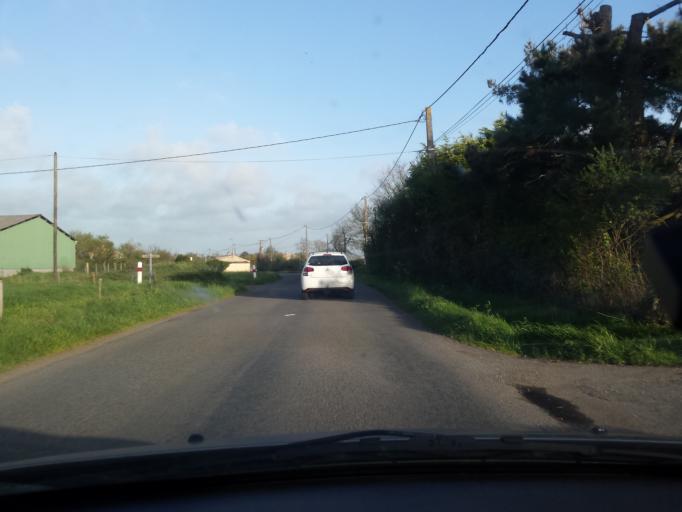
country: FR
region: Pays de la Loire
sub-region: Departement de la Vendee
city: Saint-Mathurin
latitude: 46.5664
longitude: -1.7317
